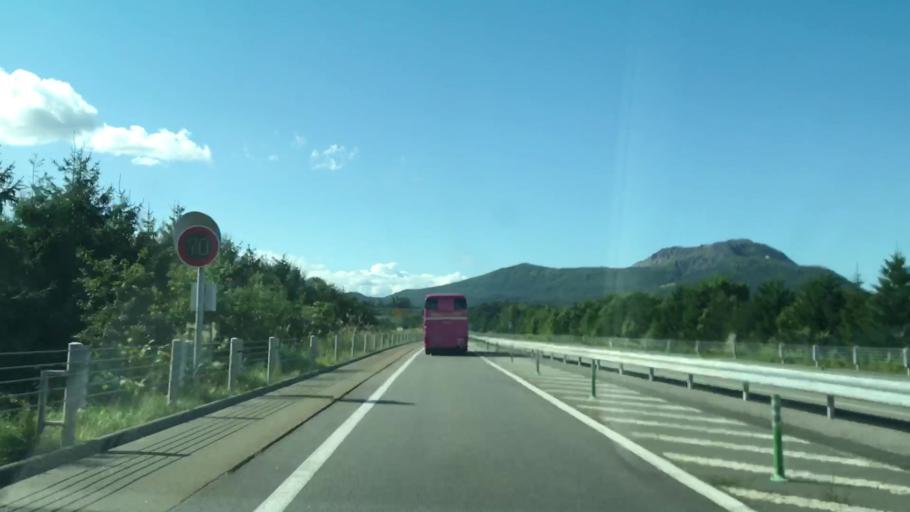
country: JP
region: Hokkaido
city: Date
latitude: 42.4916
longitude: 140.8782
